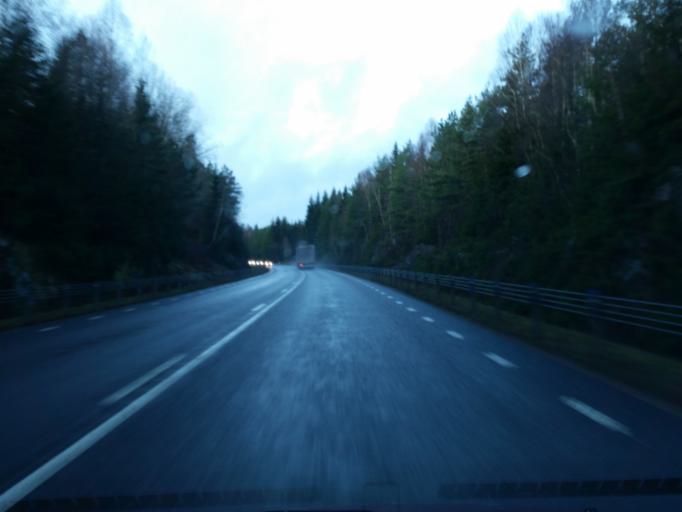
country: SE
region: Joenkoeping
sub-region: Gislaveds Kommun
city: Gislaved
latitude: 57.3351
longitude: 13.5172
